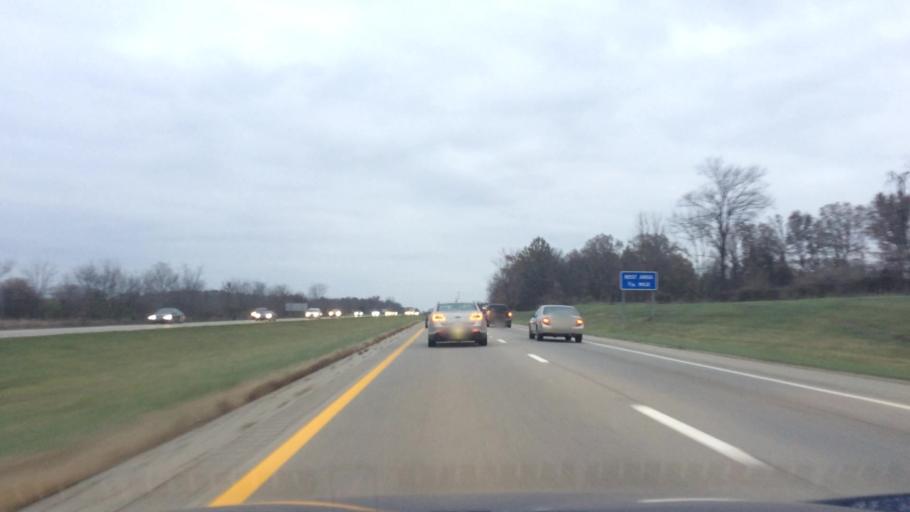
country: US
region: Ohio
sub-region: Union County
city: Marysville
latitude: 40.2101
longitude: -83.3003
